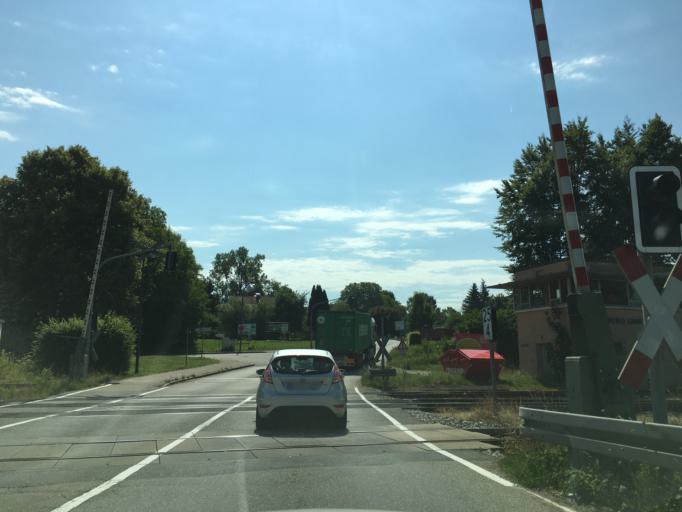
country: DE
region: Bavaria
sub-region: Upper Bavaria
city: Edling
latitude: 48.0592
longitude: 12.1840
